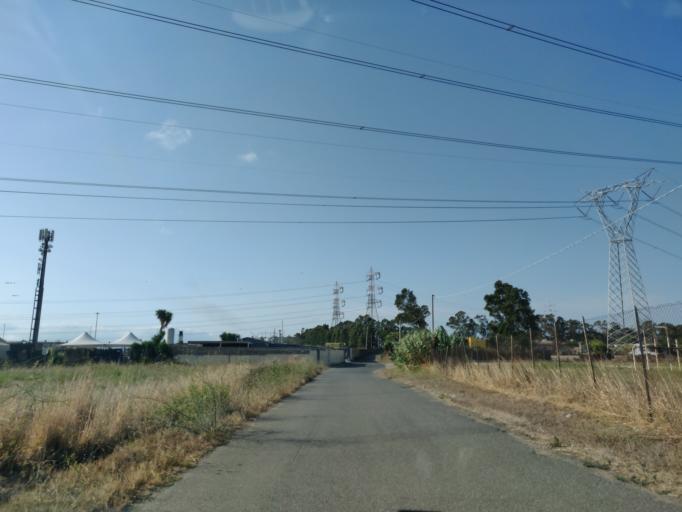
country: IT
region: Latium
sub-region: Citta metropolitana di Roma Capitale
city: Aurelia
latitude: 42.1287
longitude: 11.7674
